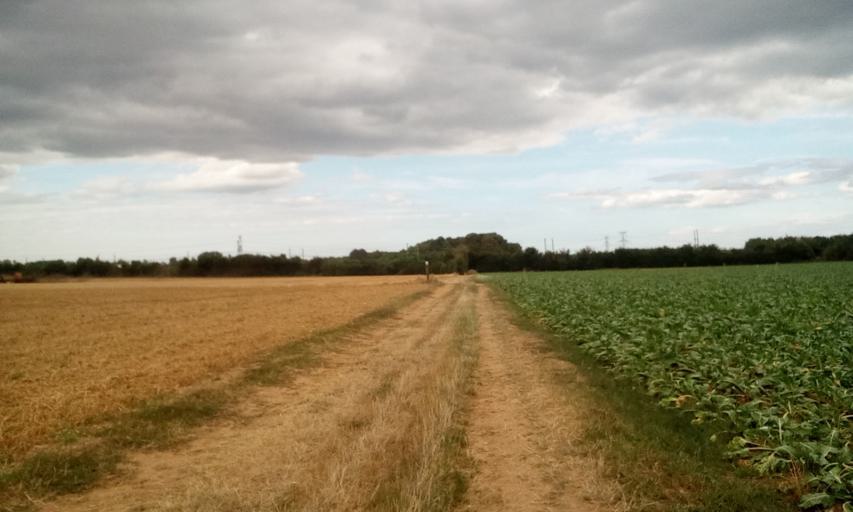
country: FR
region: Lower Normandy
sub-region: Departement du Calvados
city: Bellengreville
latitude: 49.1236
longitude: -0.2237
